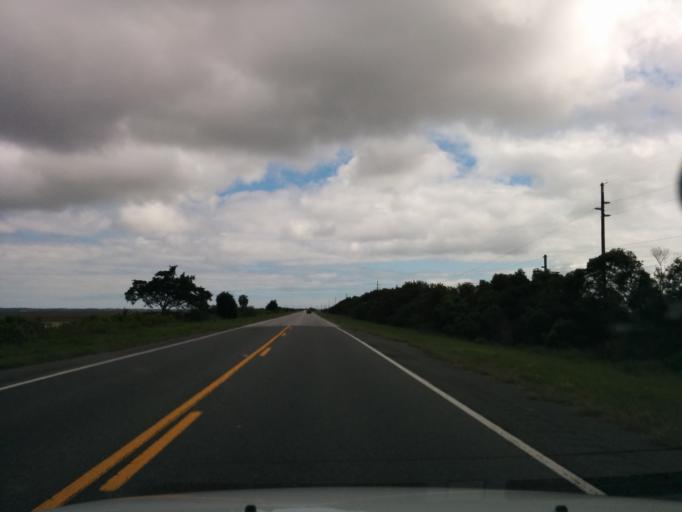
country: US
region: Georgia
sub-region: Glynn County
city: Brunswick
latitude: 31.0862
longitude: -81.4778
